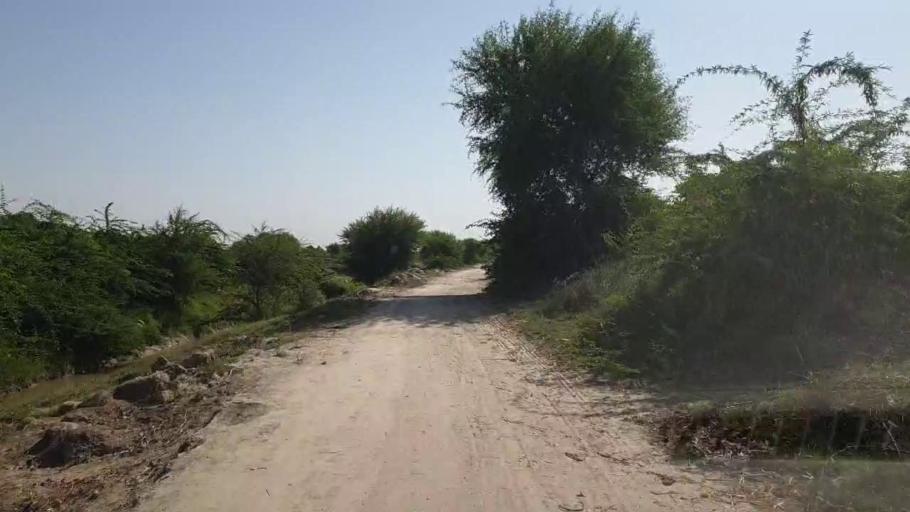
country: PK
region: Sindh
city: Kadhan
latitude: 24.6314
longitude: 68.9930
